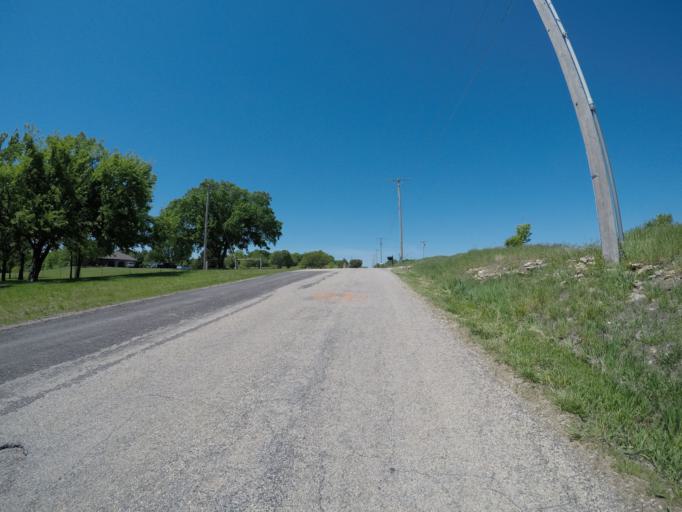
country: US
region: Kansas
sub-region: Shawnee County
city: Topeka
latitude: 39.0225
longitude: -95.5514
